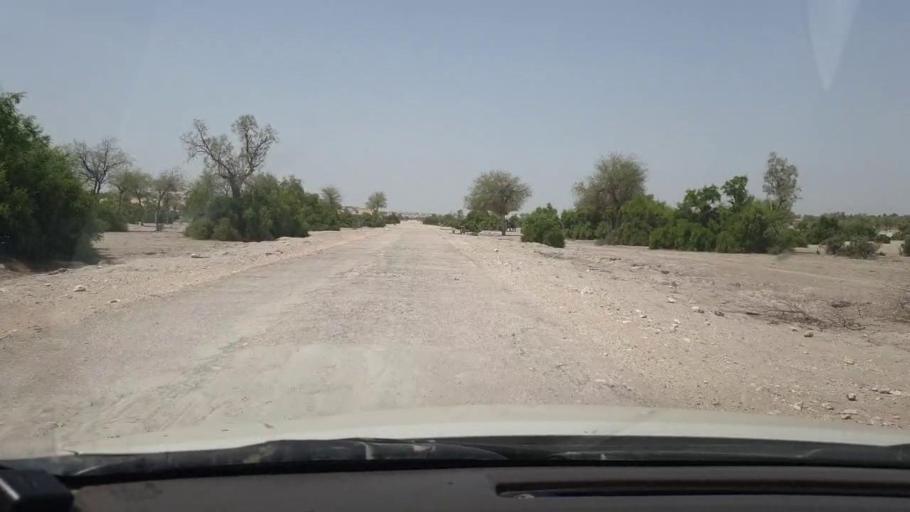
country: PK
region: Sindh
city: Rohri
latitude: 27.3008
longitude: 69.2775
